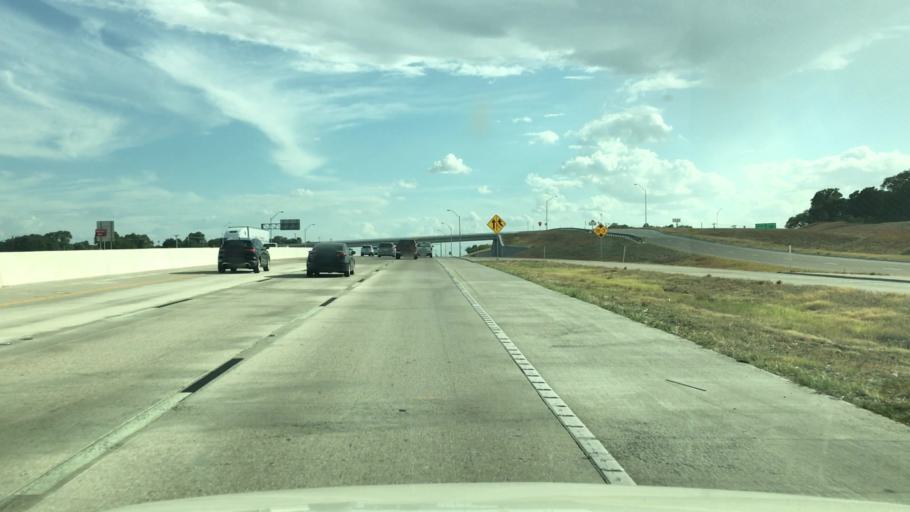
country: US
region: Texas
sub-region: Bell County
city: Belton
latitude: 31.0003
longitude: -97.4932
